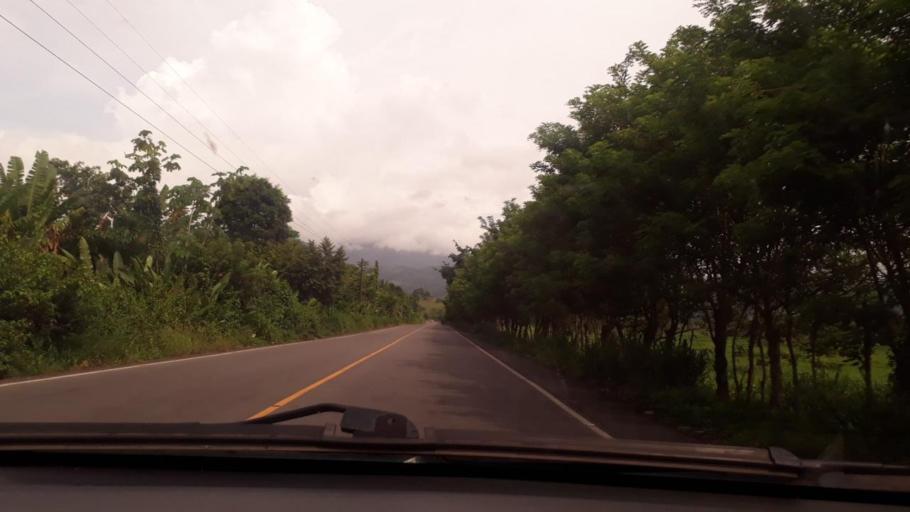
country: HN
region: Cortes
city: Potrerillos
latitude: 15.6027
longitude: -88.3838
